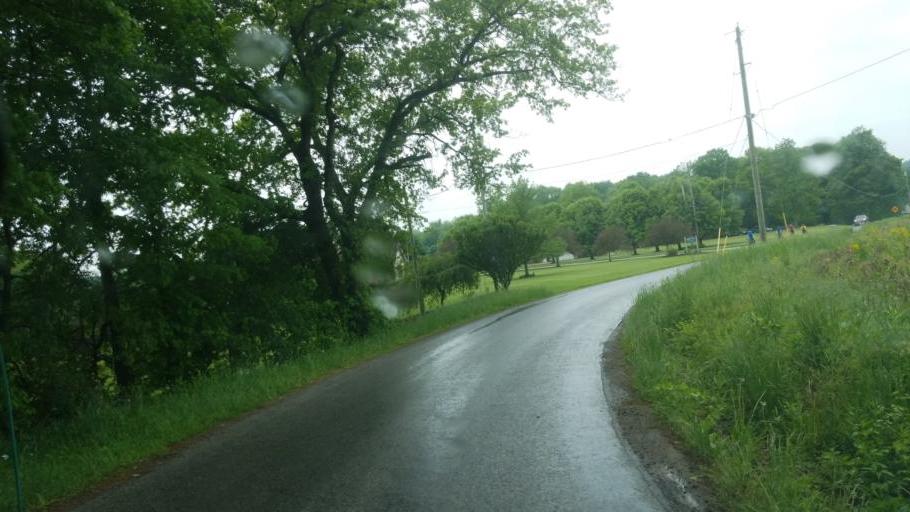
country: US
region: Ohio
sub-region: Wayne County
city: Dalton
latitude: 40.7851
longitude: -81.7221
